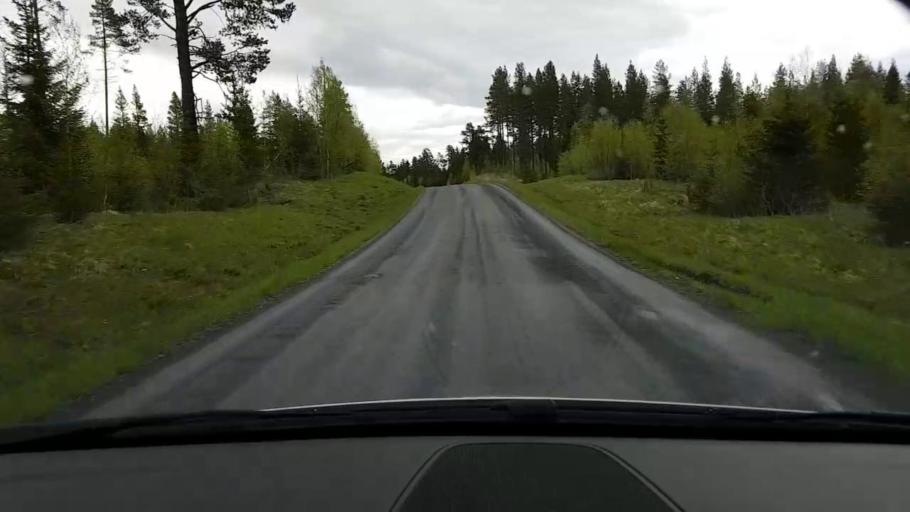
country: SE
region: Jaemtland
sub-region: Krokoms Kommun
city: Valla
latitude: 63.3044
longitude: 13.9359
